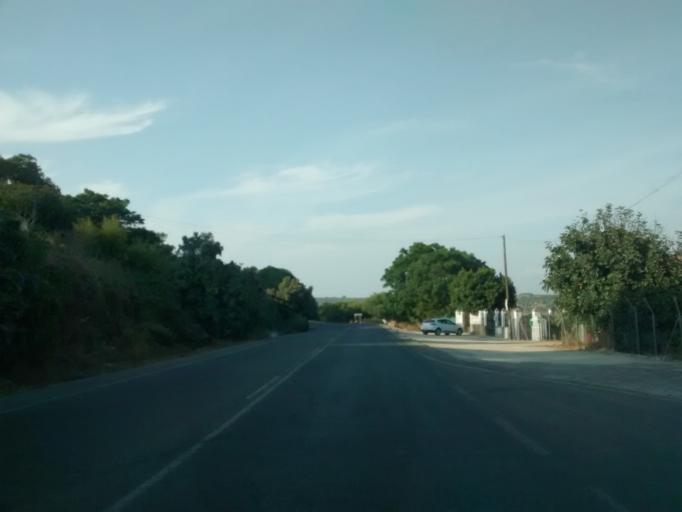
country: ES
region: Andalusia
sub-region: Provincia de Cadiz
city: Vejer de la Frontera
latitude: 36.2248
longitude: -5.9485
